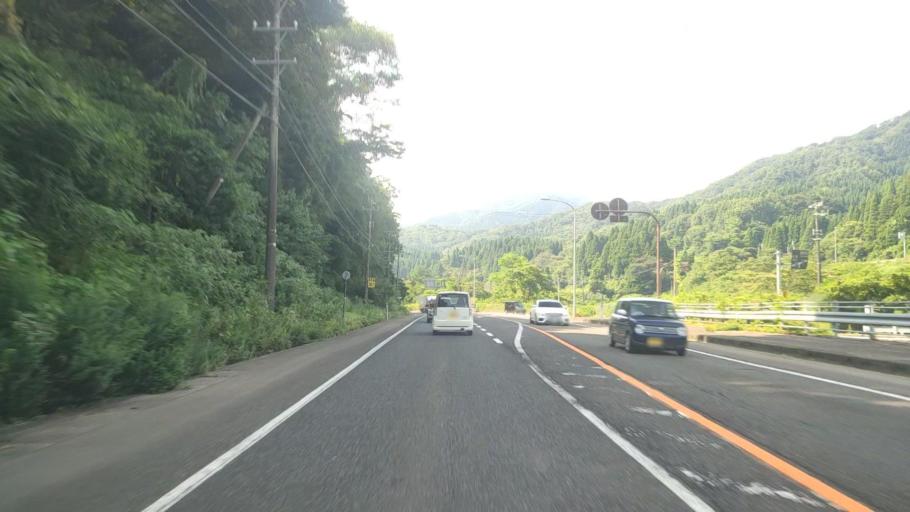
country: JP
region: Fukui
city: Tsuruga
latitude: 35.6066
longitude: 136.1214
